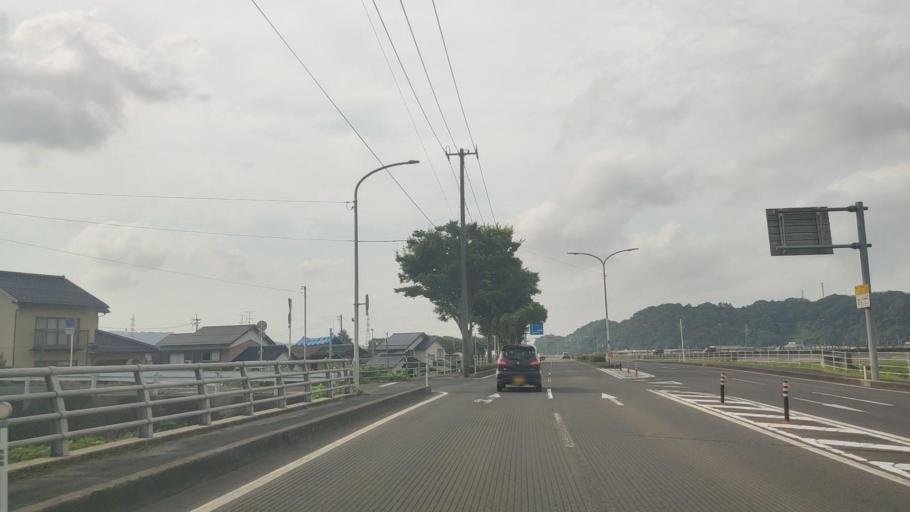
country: JP
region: Tottori
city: Kurayoshi
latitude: 35.4217
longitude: 133.8494
